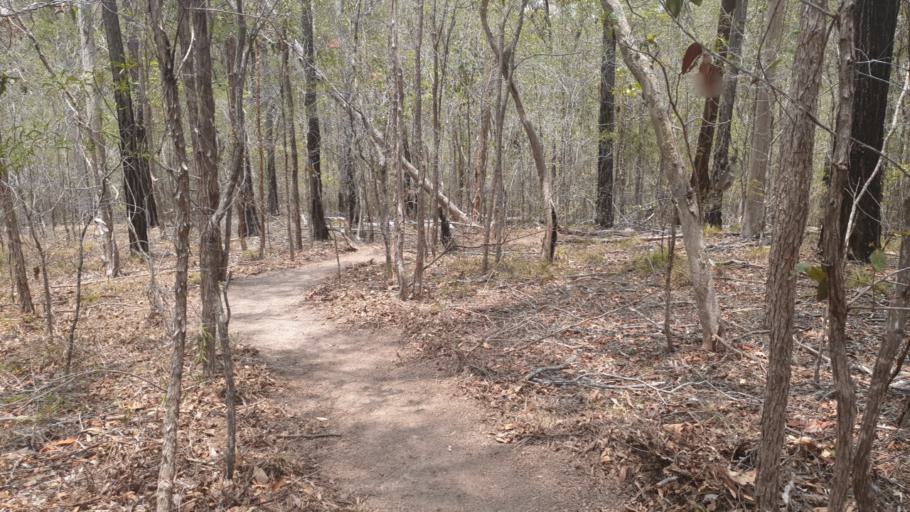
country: AU
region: Queensland
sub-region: Brisbane
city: Burbank
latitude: -27.5996
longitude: 153.2139
